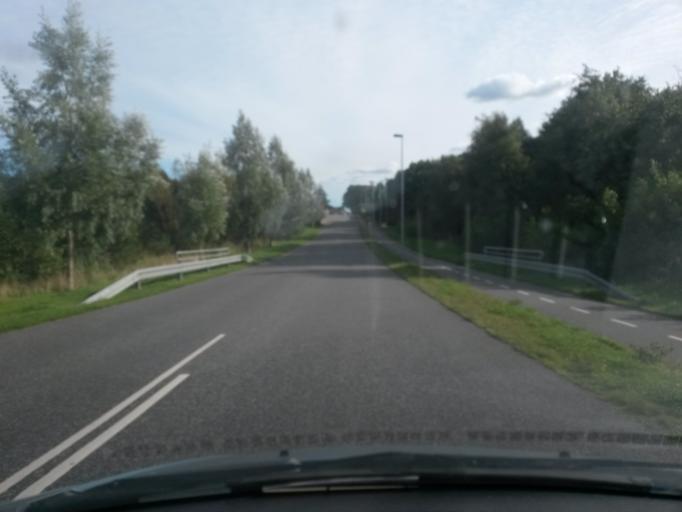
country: DK
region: Central Jutland
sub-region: Silkeborg Kommune
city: Kjellerup
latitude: 56.2960
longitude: 9.4273
